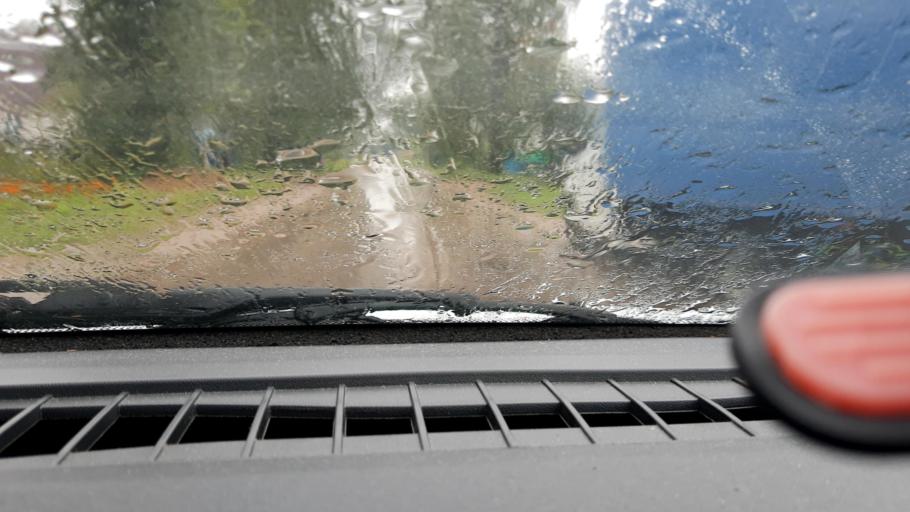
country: RU
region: Nizjnij Novgorod
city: Lyskovo
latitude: 56.0298
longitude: 45.0226
